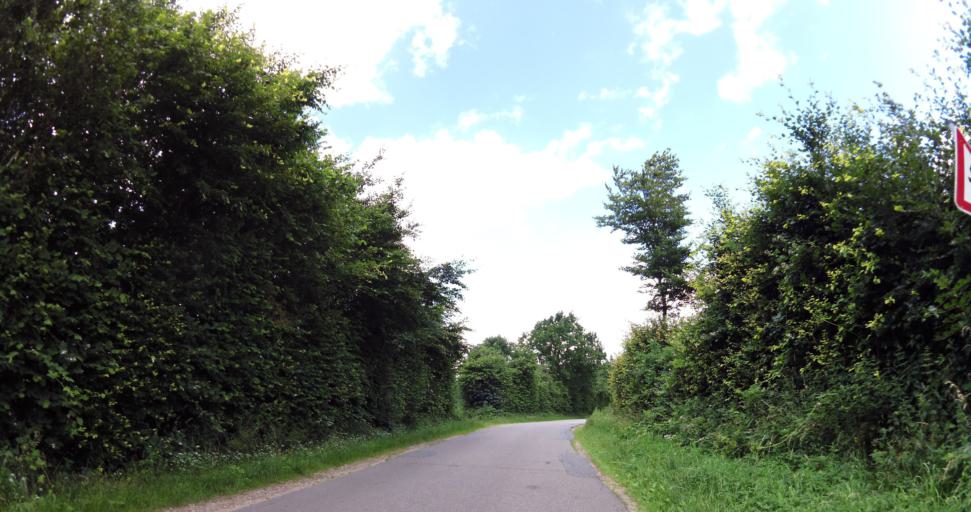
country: DE
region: Schleswig-Holstein
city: Brodersby
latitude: 54.5041
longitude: 9.7229
